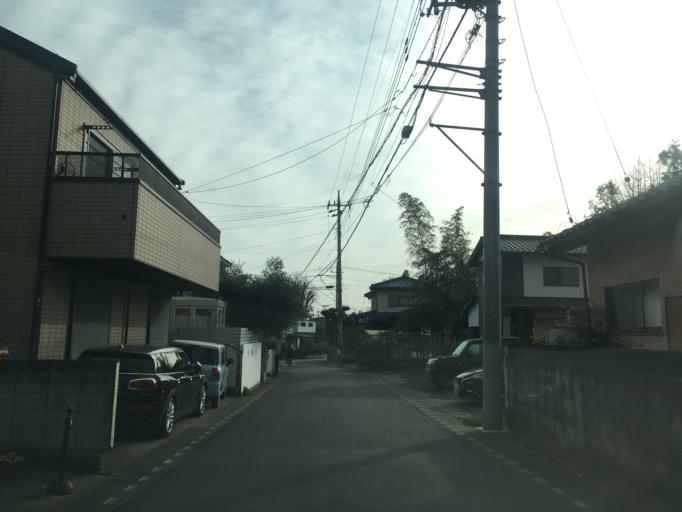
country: JP
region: Tokyo
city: Higashimurayama-shi
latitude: 35.7737
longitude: 139.4303
